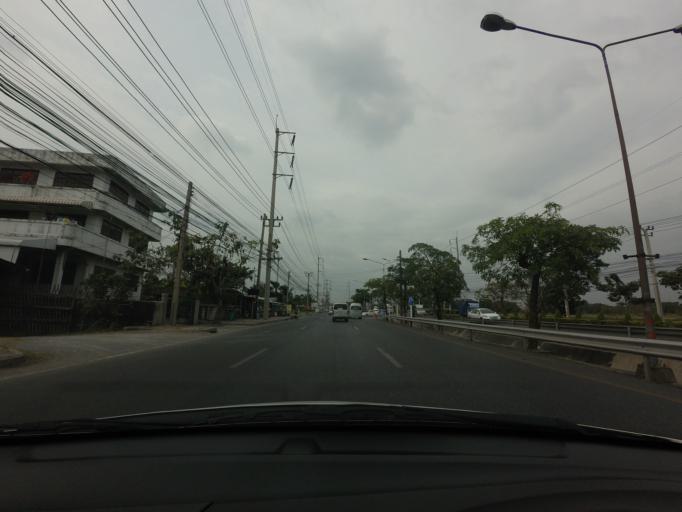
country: TH
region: Samut Prakan
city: Samut Prakan
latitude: 13.5550
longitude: 100.6137
